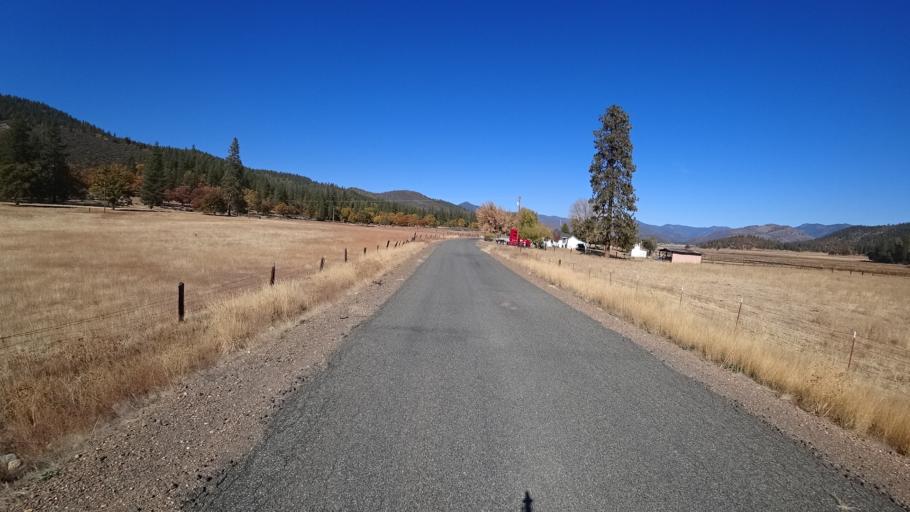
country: US
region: California
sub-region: Siskiyou County
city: Yreka
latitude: 41.5919
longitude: -122.9117
